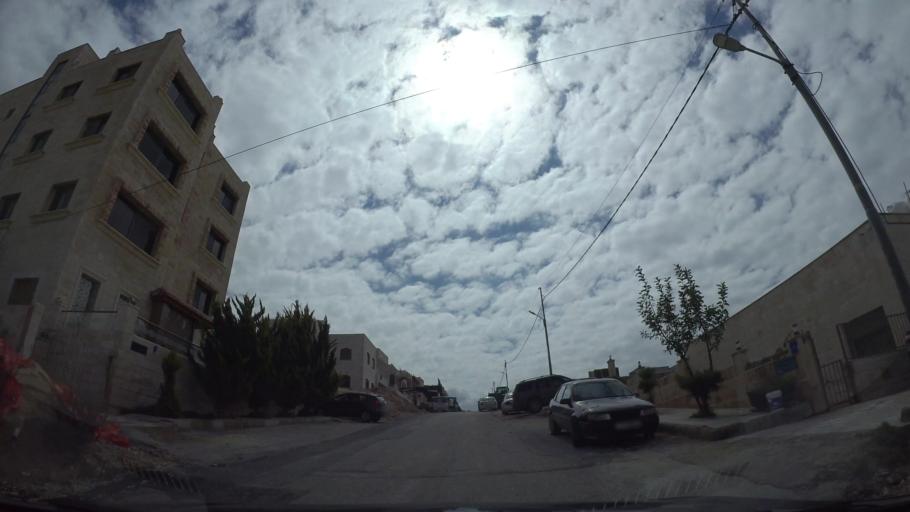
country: JO
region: Amman
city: Al Jubayhah
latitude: 32.0046
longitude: 35.9129
